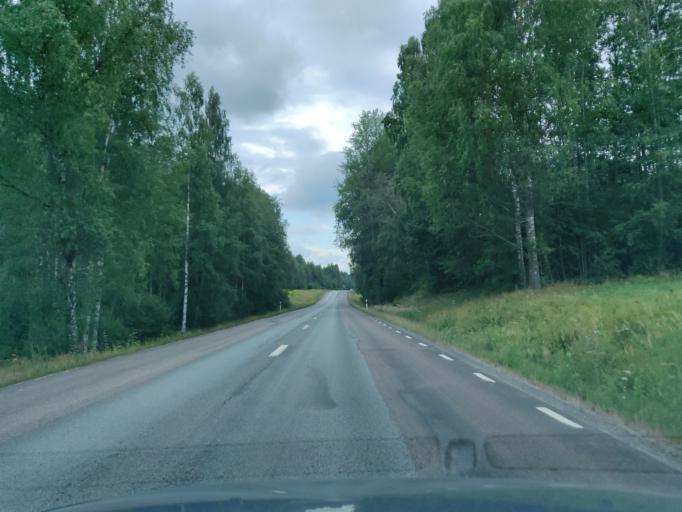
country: SE
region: Vaermland
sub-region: Munkfors Kommun
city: Munkfors
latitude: 59.8671
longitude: 13.5614
